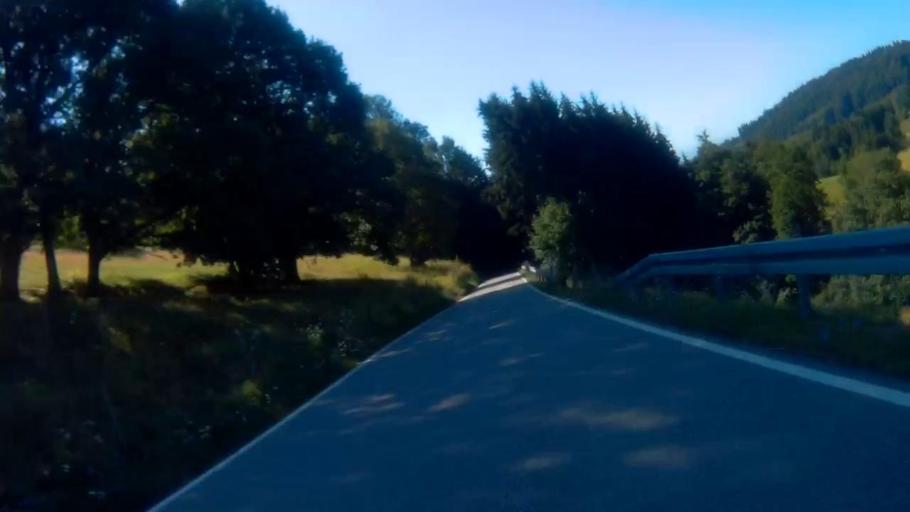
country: DE
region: Baden-Wuerttemberg
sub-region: Freiburg Region
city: Zell im Wiesental
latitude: 47.7150
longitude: 7.8406
